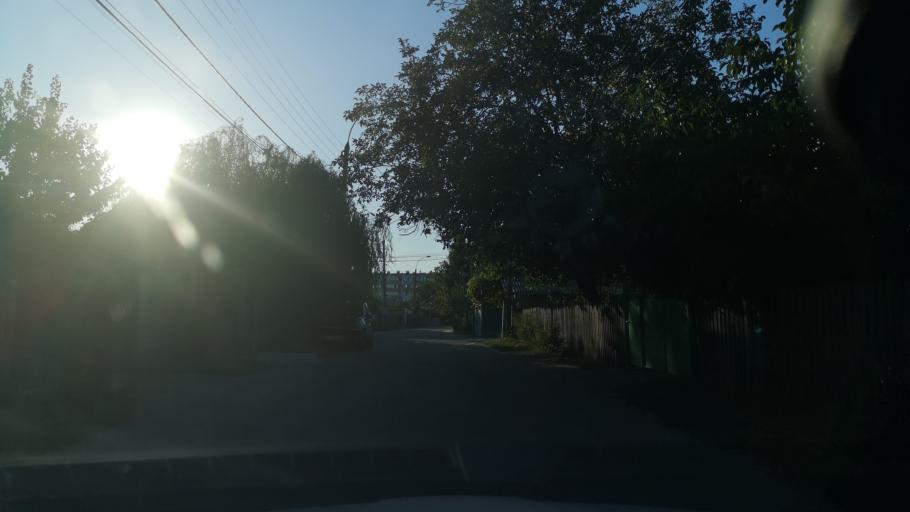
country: MD
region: Chisinau
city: Chisinau
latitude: 46.9885
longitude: 28.8790
